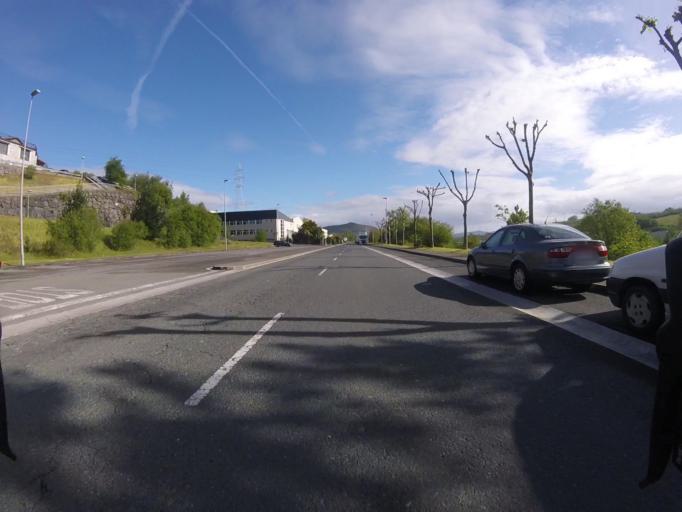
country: ES
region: Basque Country
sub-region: Provincia de Guipuzcoa
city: Urnieta
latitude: 43.2368
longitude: -1.9954
